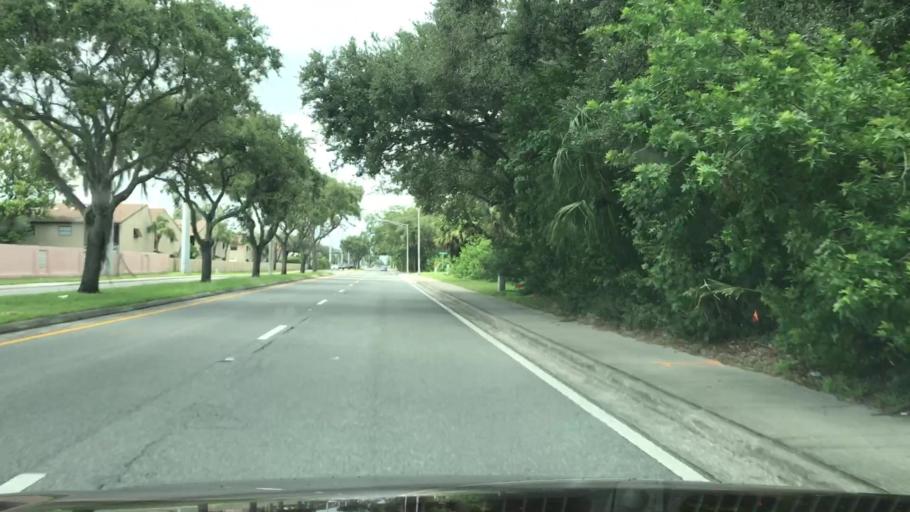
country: US
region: Florida
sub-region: Sarasota County
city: Gulf Gate Estates
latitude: 27.2482
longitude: -82.4975
